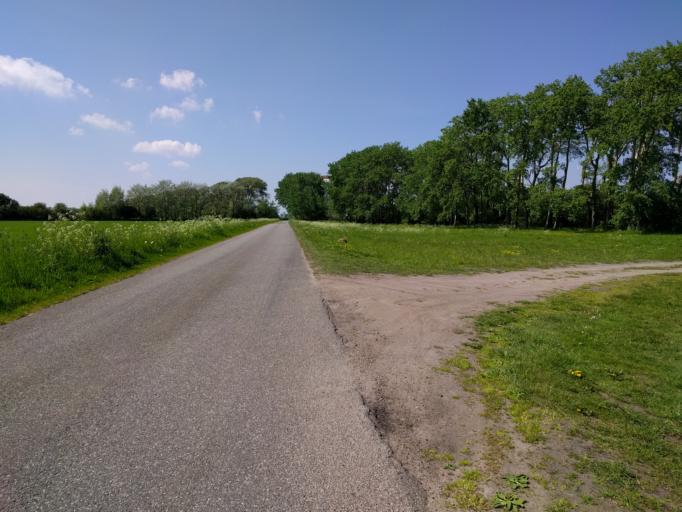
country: DK
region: Zealand
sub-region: Guldborgsund Kommune
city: Stubbekobing
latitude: 54.8862
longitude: 12.1184
